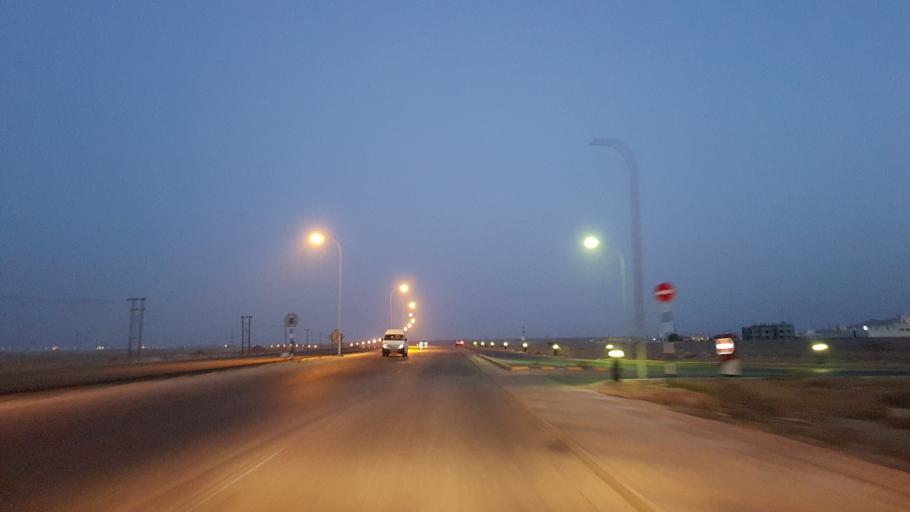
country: OM
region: Ash Sharqiyah
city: Sur
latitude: 22.5941
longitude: 59.4368
